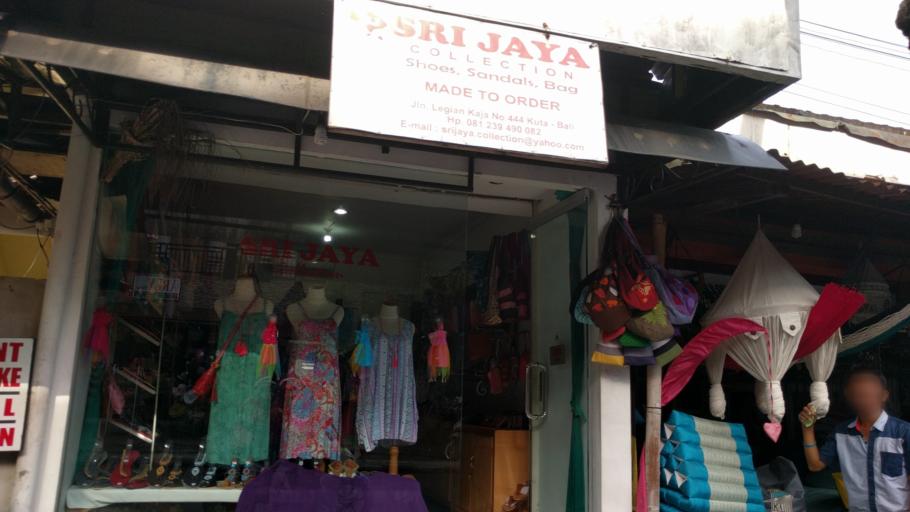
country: ID
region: Bali
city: Kuta
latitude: -8.7026
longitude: 115.1702
